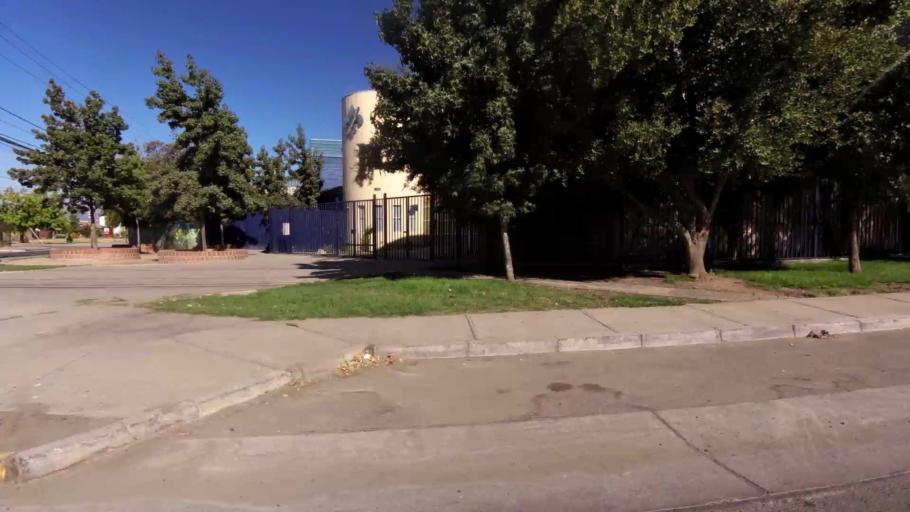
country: CL
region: O'Higgins
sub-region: Provincia de Cachapoal
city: Rancagua
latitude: -34.1819
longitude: -70.7694
